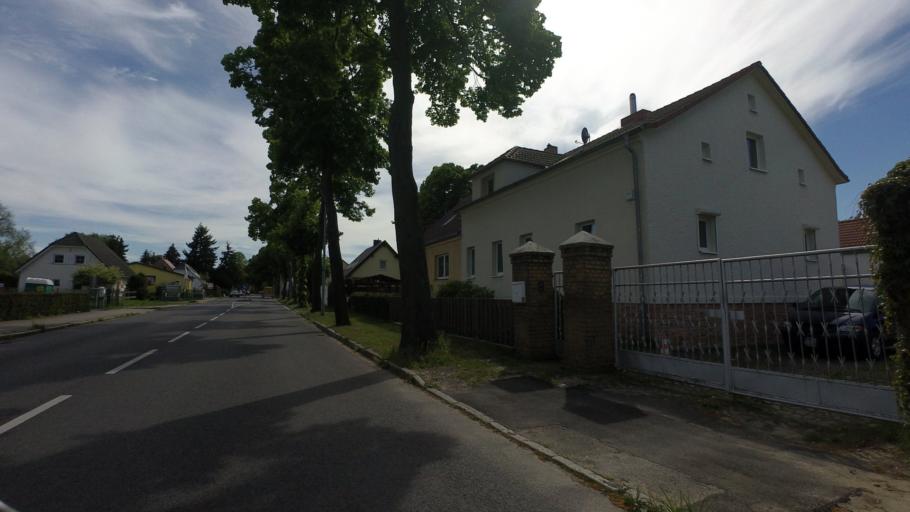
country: DE
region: Berlin
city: Lichtenrade
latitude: 52.3479
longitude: 13.4363
